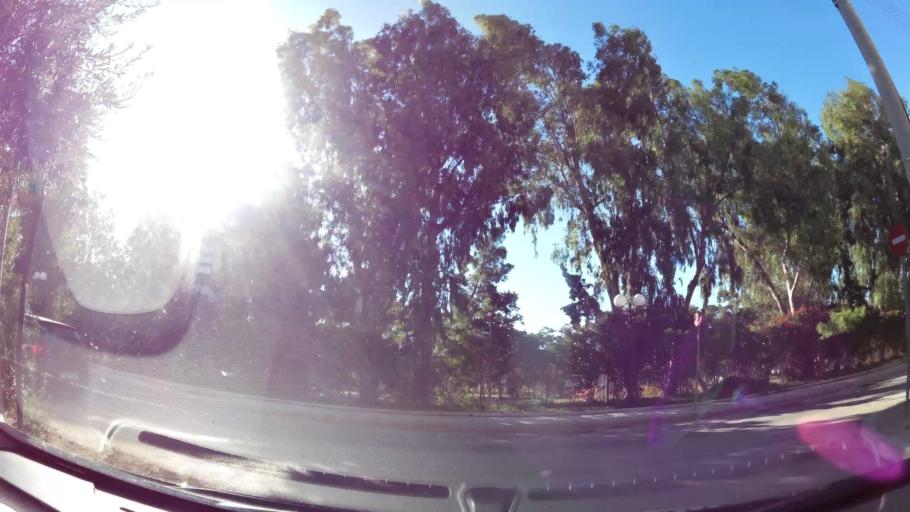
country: GR
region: Attica
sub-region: Nomarchia Athinas
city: Glyfada
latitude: 37.8490
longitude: 23.7613
